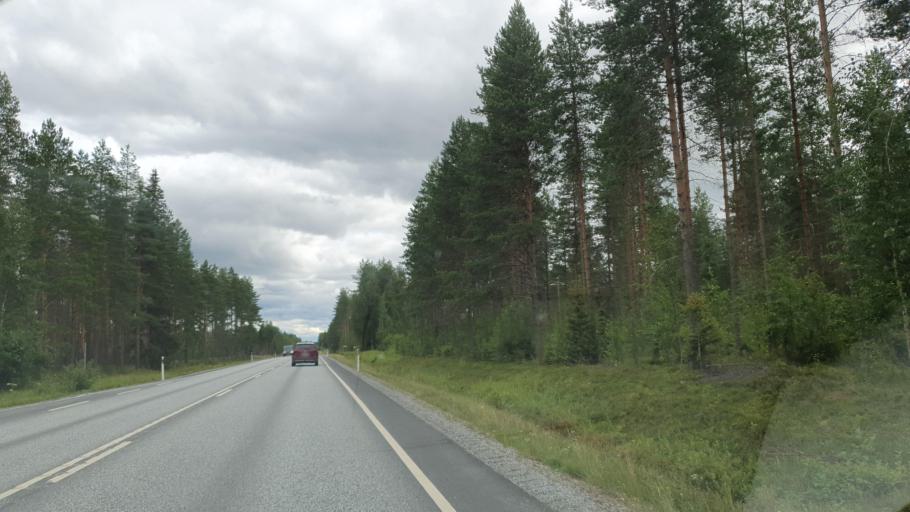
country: FI
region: Northern Savo
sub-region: Ylae-Savo
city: Sonkajaervi
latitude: 63.8951
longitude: 27.4111
